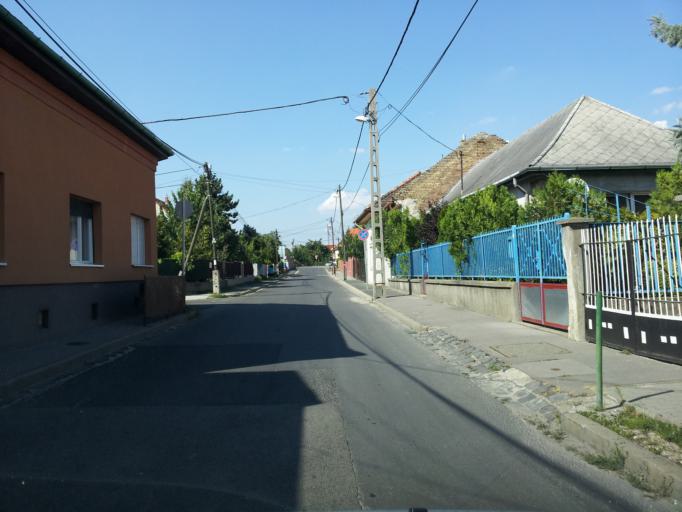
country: HU
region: Budapest
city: Budapest XXII. keruelet
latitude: 47.4209
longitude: 19.0319
